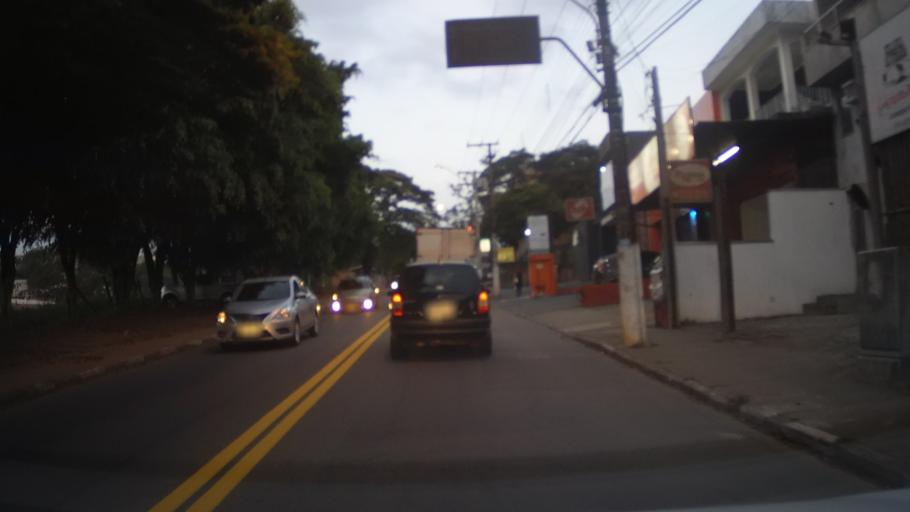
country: BR
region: Sao Paulo
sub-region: Aruja
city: Aruja
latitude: -23.3927
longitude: -46.3190
